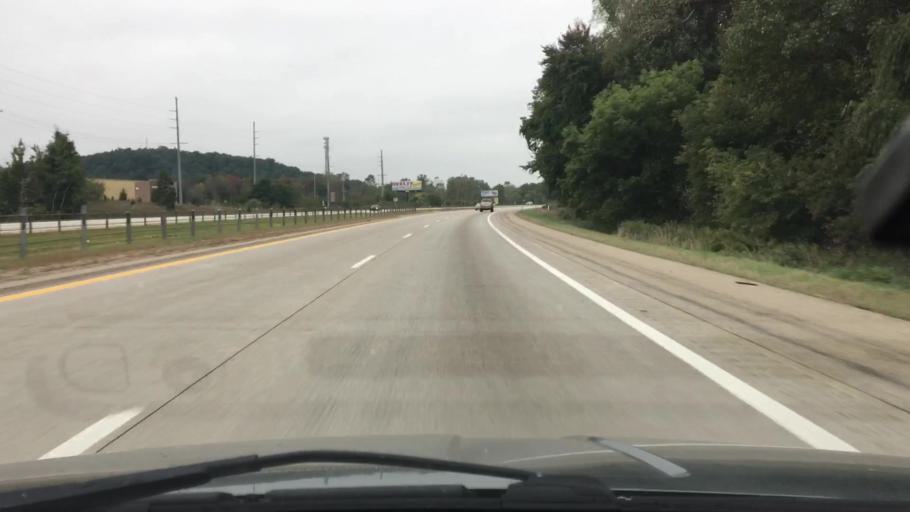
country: US
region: Michigan
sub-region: Van Buren County
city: Paw Paw
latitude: 42.2084
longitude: -85.8778
